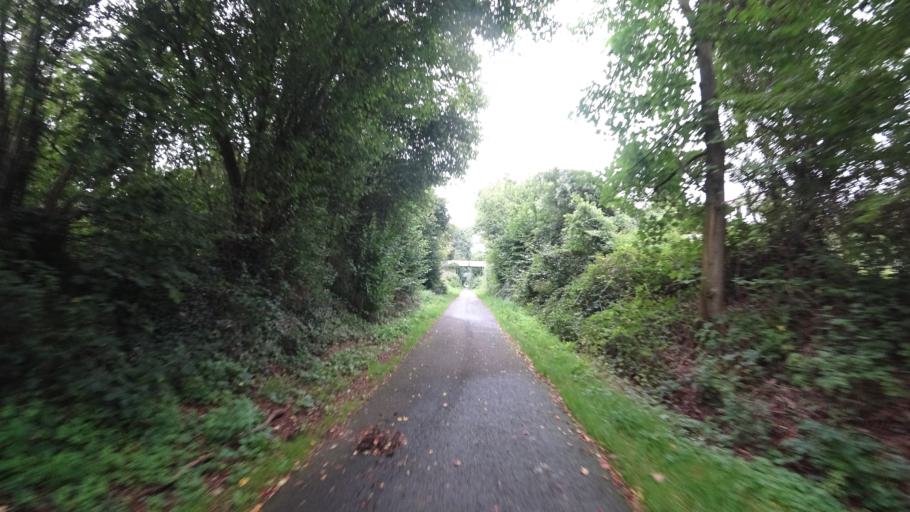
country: BE
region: Wallonia
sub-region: Province de Namur
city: Namur
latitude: 50.5016
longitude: 4.8679
